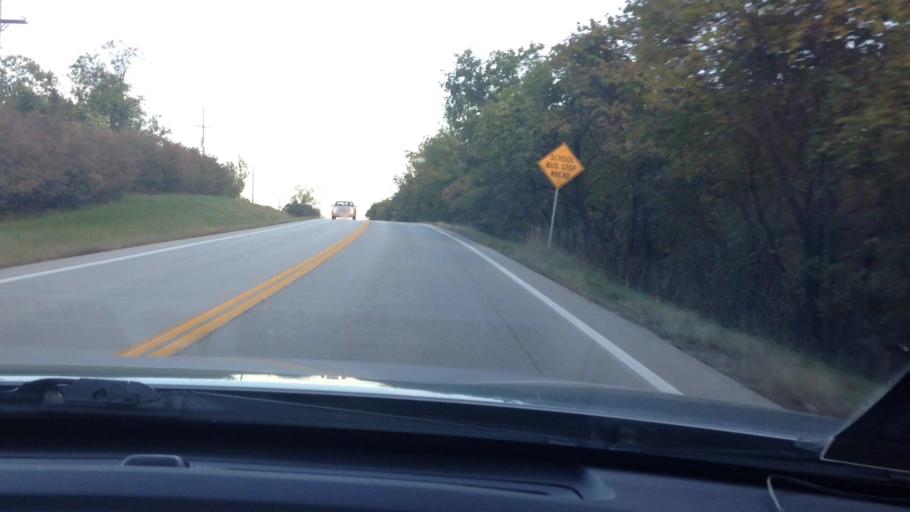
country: US
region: Missouri
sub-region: Platte County
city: Weatherby Lake
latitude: 39.2267
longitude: -94.7743
